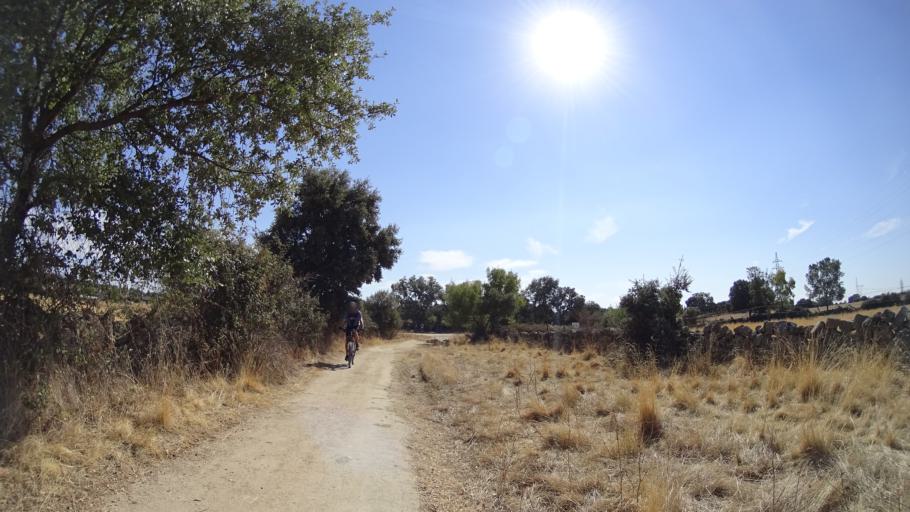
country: ES
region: Madrid
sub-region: Provincia de Madrid
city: Collado-Villalba
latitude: 40.6138
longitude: -4.0210
